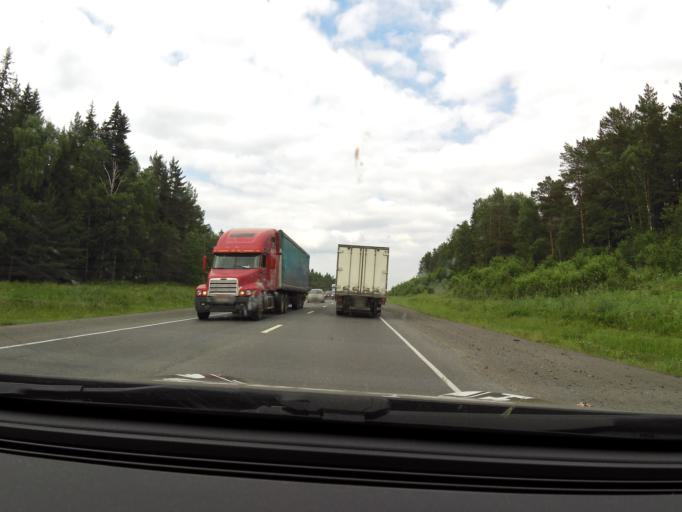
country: RU
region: Sverdlovsk
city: Druzhinino
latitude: 56.8156
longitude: 59.5612
